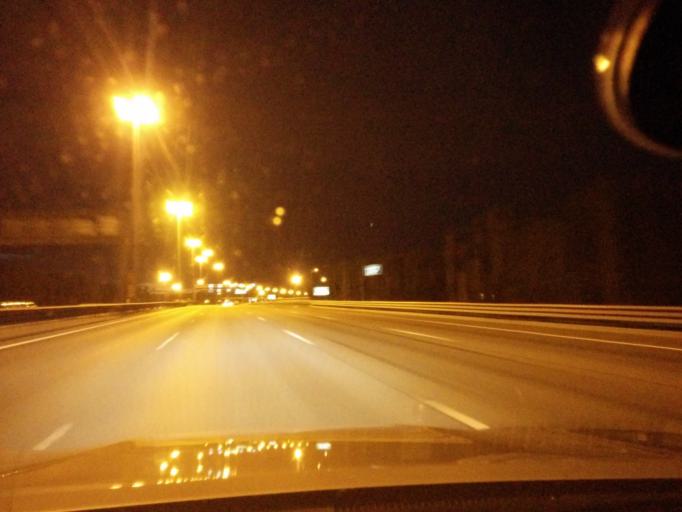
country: RU
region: St.-Petersburg
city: Krasnogvargeisky
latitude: 59.9392
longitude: 30.5391
